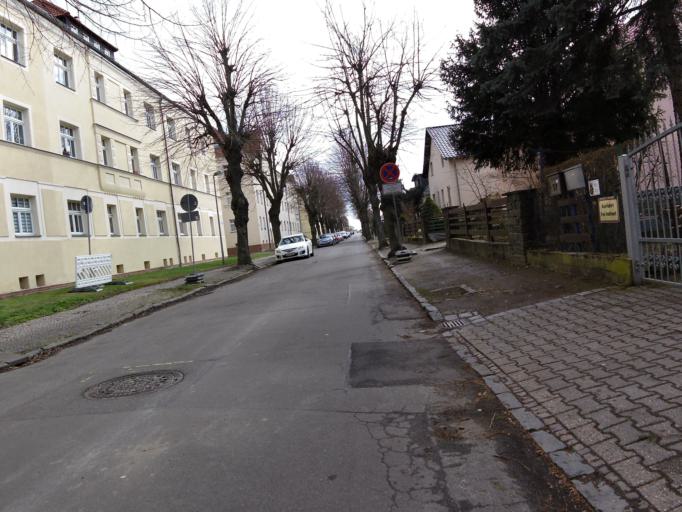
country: DE
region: Saxony
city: Taucha
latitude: 51.3354
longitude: 12.4734
